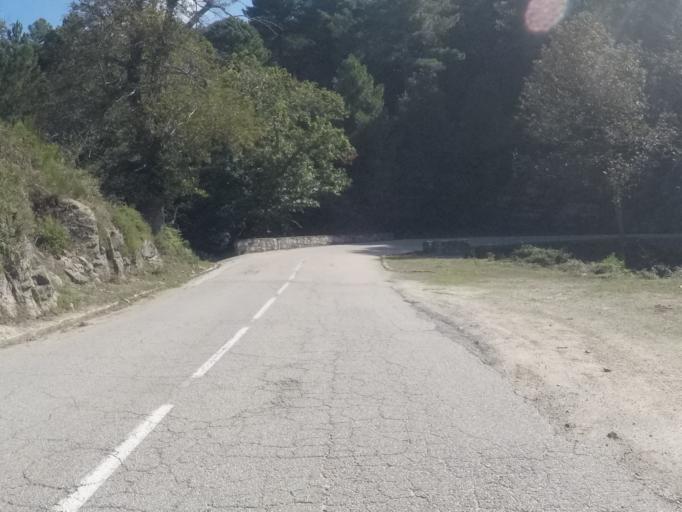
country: FR
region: Corsica
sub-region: Departement de la Corse-du-Sud
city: Zonza
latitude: 41.7661
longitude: 9.0881
